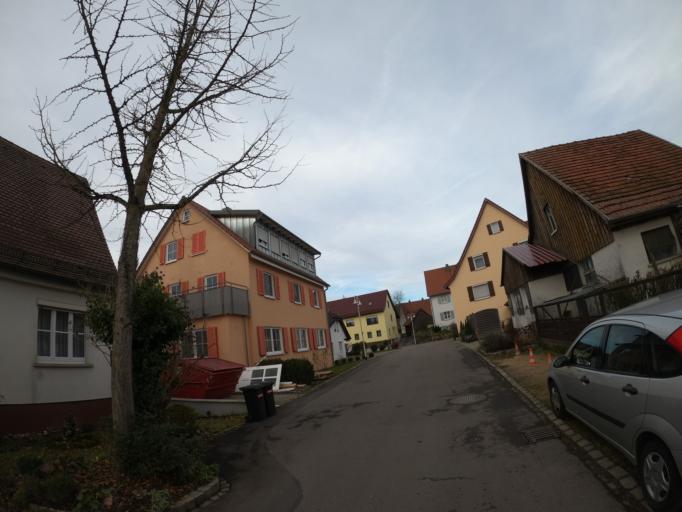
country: DE
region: Baden-Wuerttemberg
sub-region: Regierungsbezirk Stuttgart
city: Ottenbach
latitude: 48.7368
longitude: 9.7467
